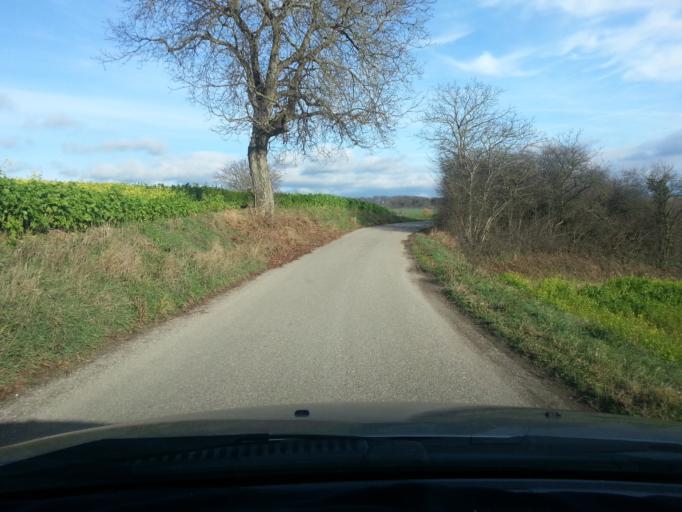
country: DE
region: Baden-Wuerttemberg
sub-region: Karlsruhe Region
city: Ostringen
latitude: 49.2059
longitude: 8.7336
